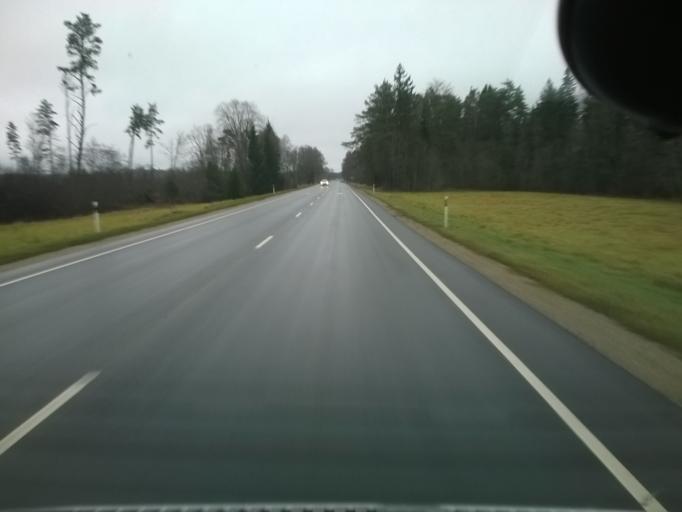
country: EE
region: Harju
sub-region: Nissi vald
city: Turba
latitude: 59.0119
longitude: 24.1339
